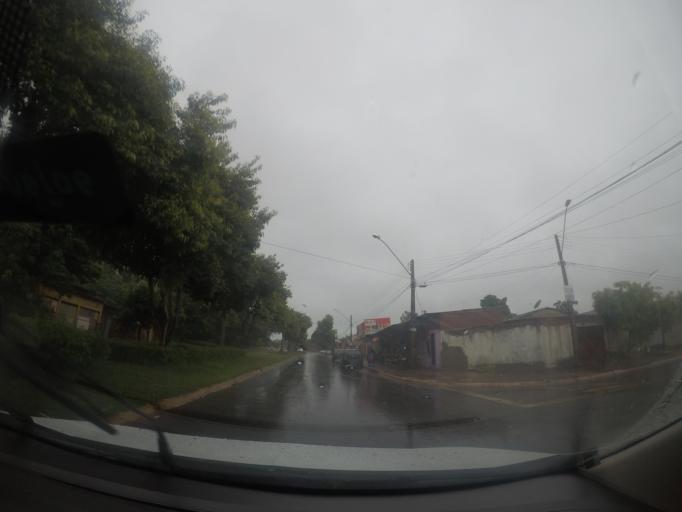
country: BR
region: Goias
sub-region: Goiania
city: Goiania
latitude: -16.6037
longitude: -49.3425
